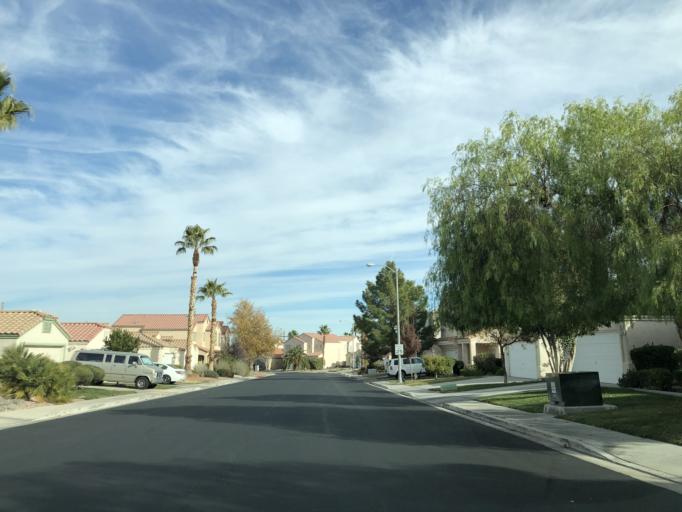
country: US
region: Nevada
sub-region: Clark County
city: Whitney
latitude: 36.0134
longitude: -115.0950
